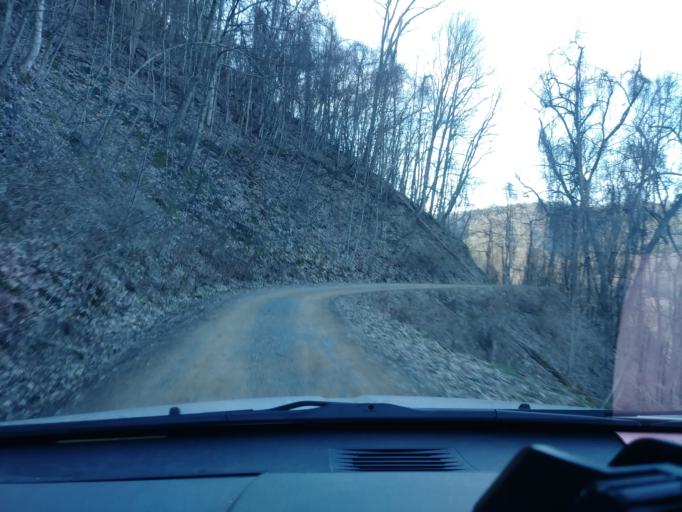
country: US
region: Tennessee
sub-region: Greene County
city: Tusculum
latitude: 36.0680
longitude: -82.6831
